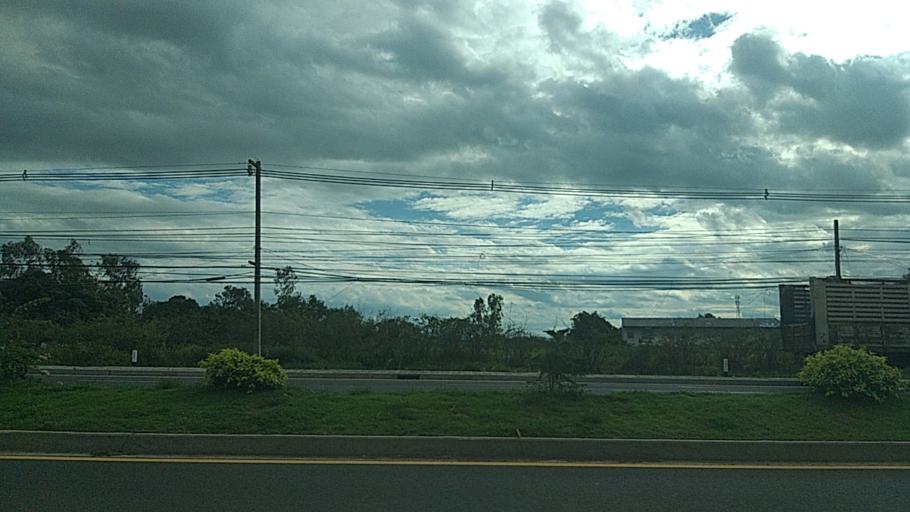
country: TH
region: Surin
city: Prasat
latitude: 14.6249
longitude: 103.4107
